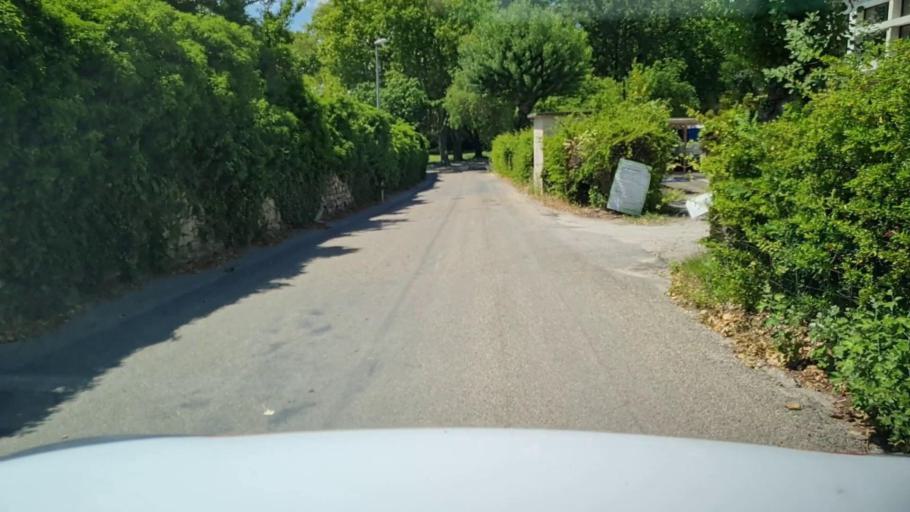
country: FR
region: Languedoc-Roussillon
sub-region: Departement du Gard
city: Saint-Mamert-du-Gard
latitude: 43.8981
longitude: 4.2134
